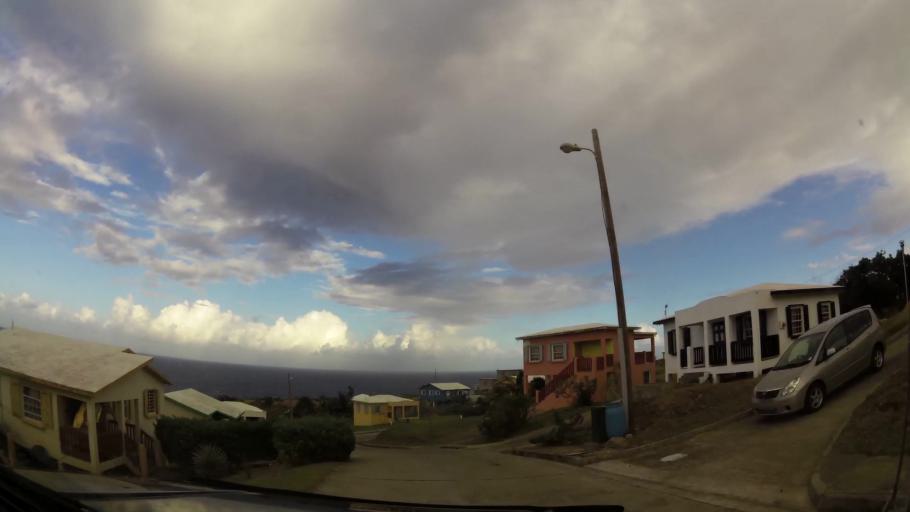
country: MS
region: Saint Peter
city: Brades
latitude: 16.7952
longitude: -62.1817
